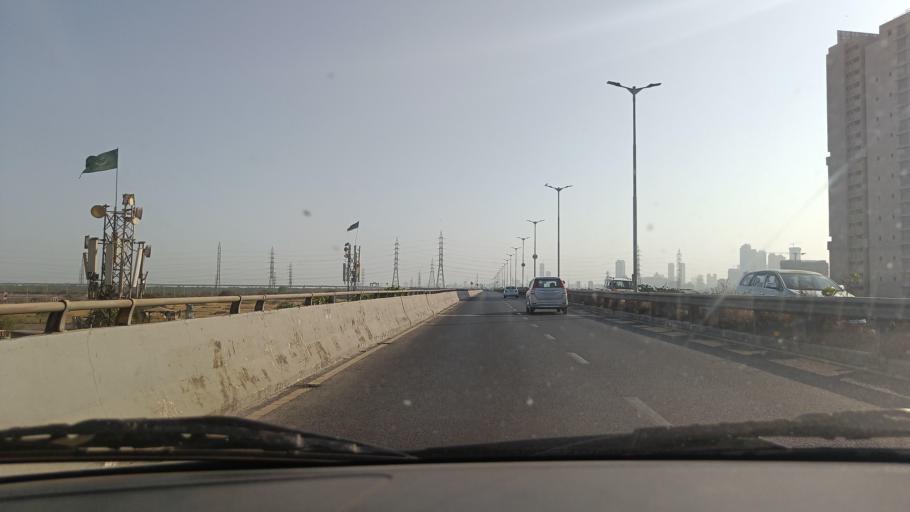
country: IN
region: Maharashtra
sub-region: Mumbai Suburban
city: Mumbai
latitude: 19.0214
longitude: 72.8755
